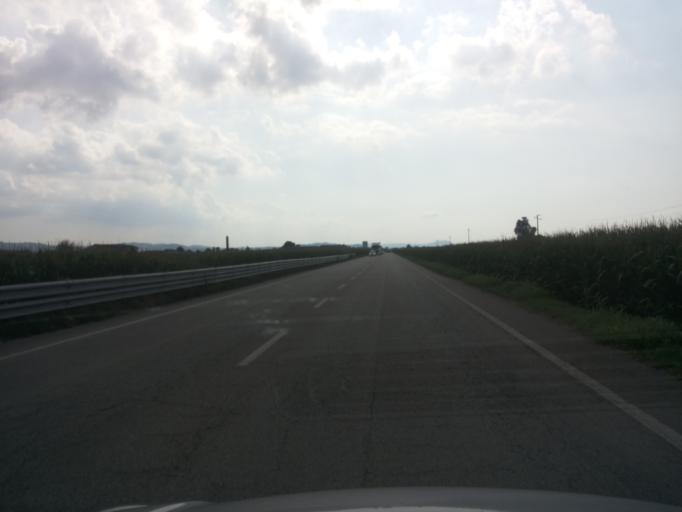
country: IT
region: Piedmont
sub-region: Provincia di Alessandria
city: Villanova Monferrato
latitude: 45.1614
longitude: 8.4758
